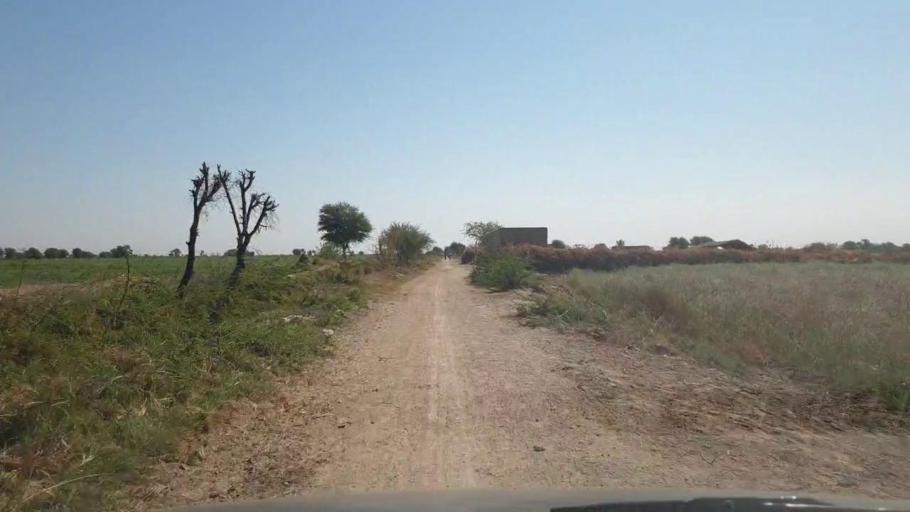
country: PK
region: Sindh
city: Umarkot
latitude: 25.3817
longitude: 69.6259
